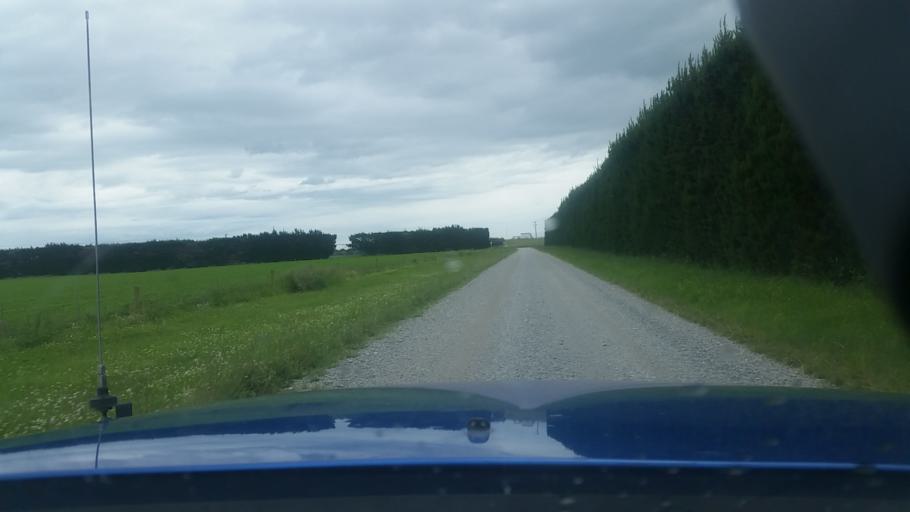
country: NZ
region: Canterbury
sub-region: Ashburton District
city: Rakaia
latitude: -43.9036
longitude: 172.0574
